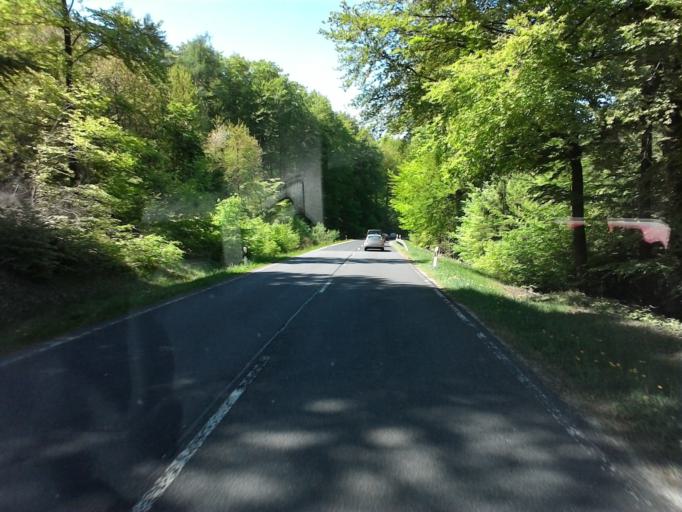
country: DE
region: Bavaria
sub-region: Regierungsbezirk Unterfranken
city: Rothenbuch
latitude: 49.9929
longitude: 9.3847
